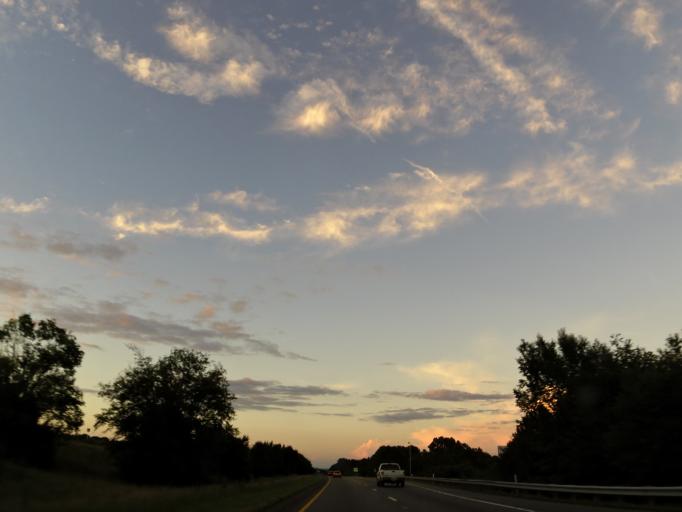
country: US
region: Tennessee
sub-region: Loudon County
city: Loudon
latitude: 35.7277
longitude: -84.3990
